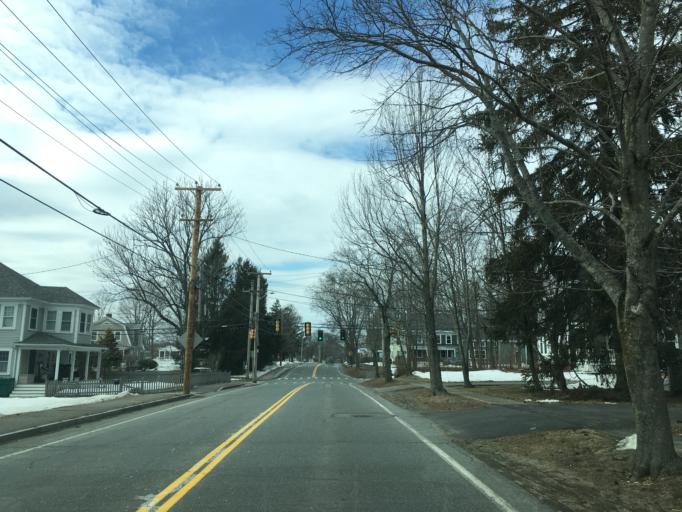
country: US
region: New Hampshire
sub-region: Rockingham County
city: Hampton
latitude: 42.9393
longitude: -70.8289
